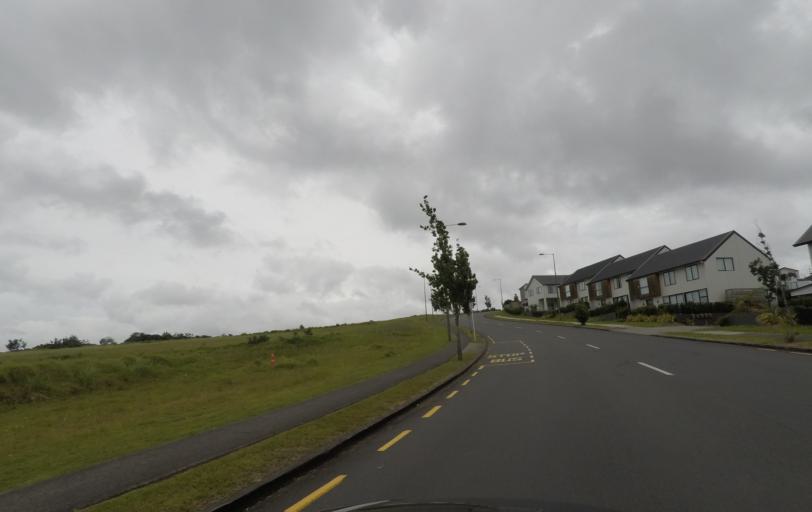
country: NZ
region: Auckland
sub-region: Auckland
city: Rosebank
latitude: -36.8270
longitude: 174.6152
